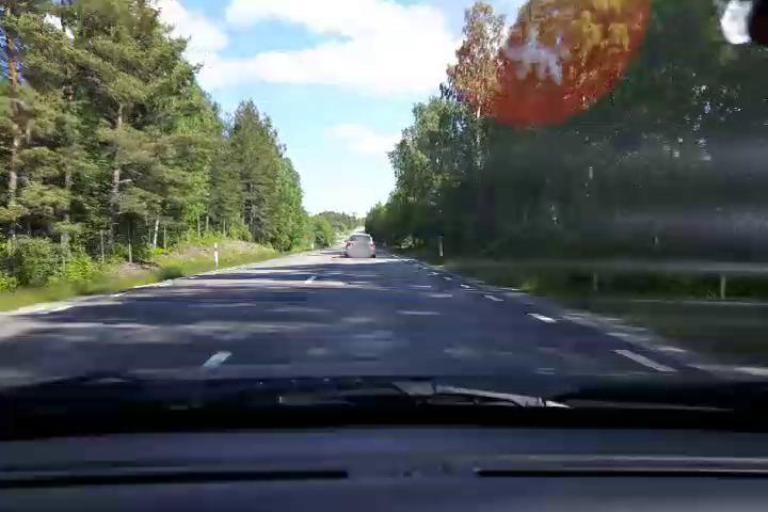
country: SE
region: Gaevleborg
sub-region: Hudiksvalls Kommun
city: Sorforsa
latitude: 61.7374
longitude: 16.9176
